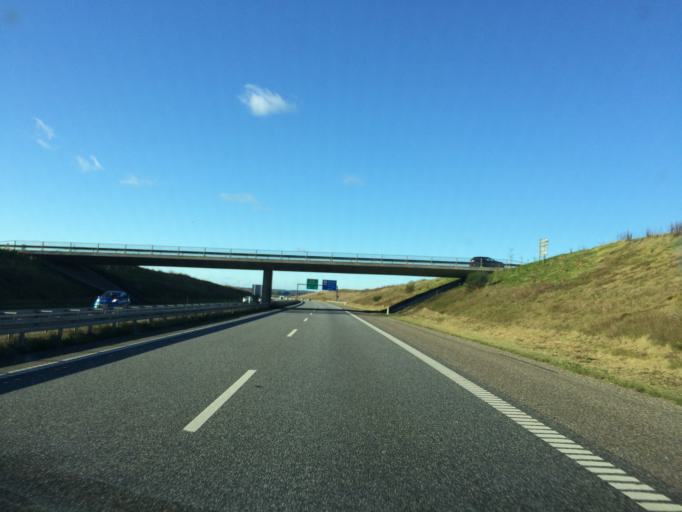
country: DK
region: Central Jutland
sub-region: Hedensted Kommune
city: Torring
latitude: 55.8255
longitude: 9.5338
